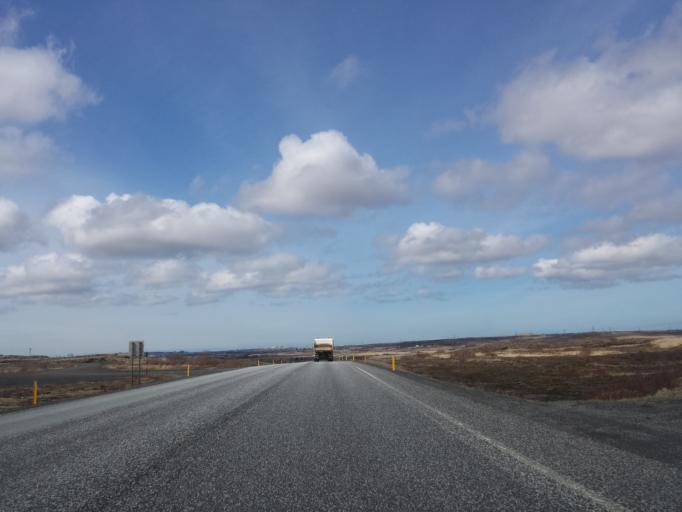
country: IS
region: Capital Region
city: Mosfellsbaer
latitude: 64.0751
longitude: -21.6449
